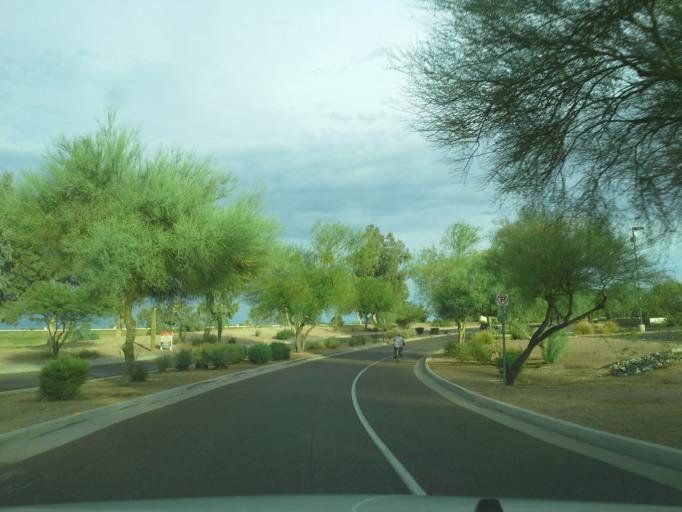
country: US
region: Arizona
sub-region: Maricopa County
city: Guadalupe
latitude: 33.3705
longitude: -111.9716
